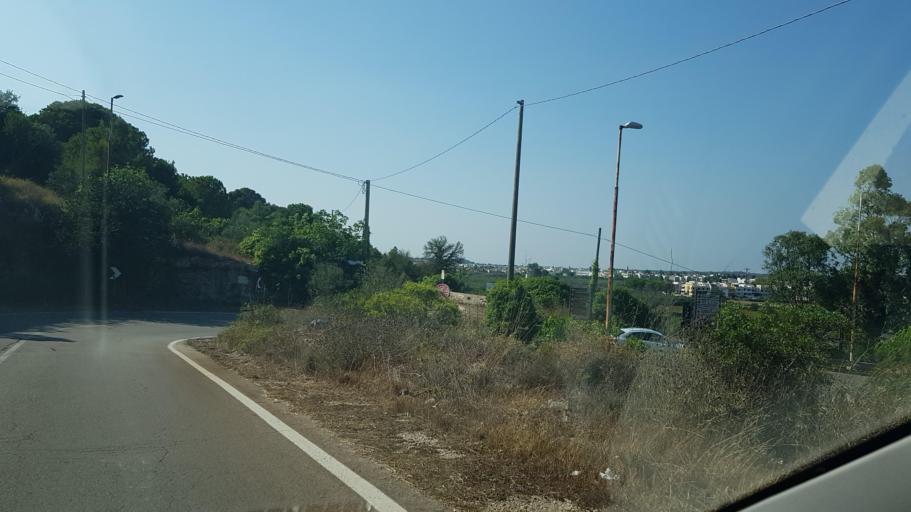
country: IT
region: Apulia
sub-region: Provincia di Lecce
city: Presicce
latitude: 39.8935
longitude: 18.2543
